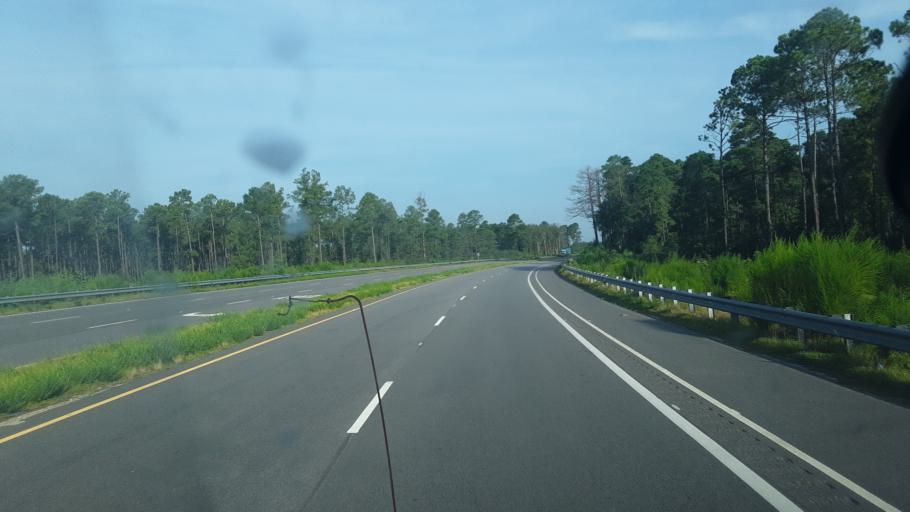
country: US
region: South Carolina
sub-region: Horry County
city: Forestbrook
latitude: 33.8063
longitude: -78.8926
